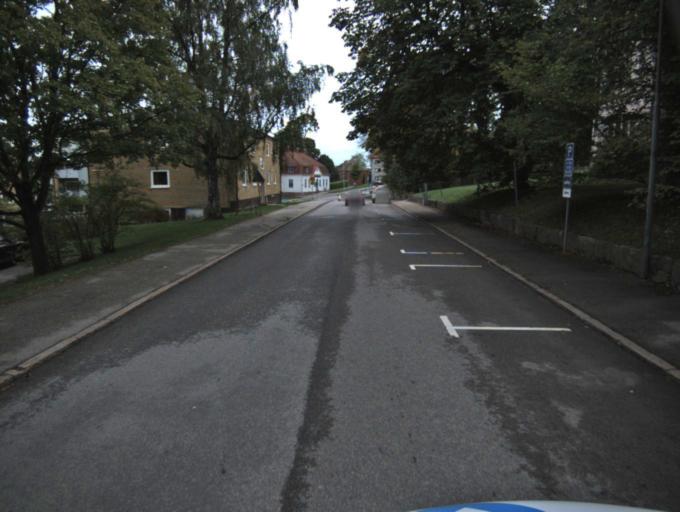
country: SE
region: Vaestra Goetaland
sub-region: Ulricehamns Kommun
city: Ulricehamn
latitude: 57.7945
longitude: 13.4168
